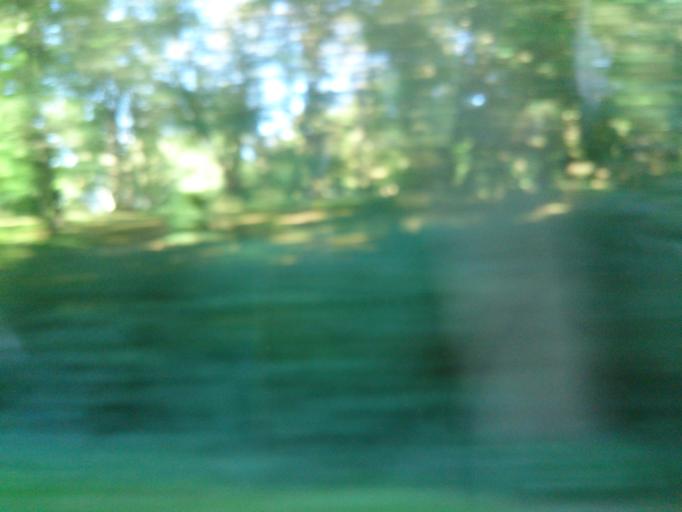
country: DE
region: Mecklenburg-Vorpommern
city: Anklam
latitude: 53.8866
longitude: 13.6770
